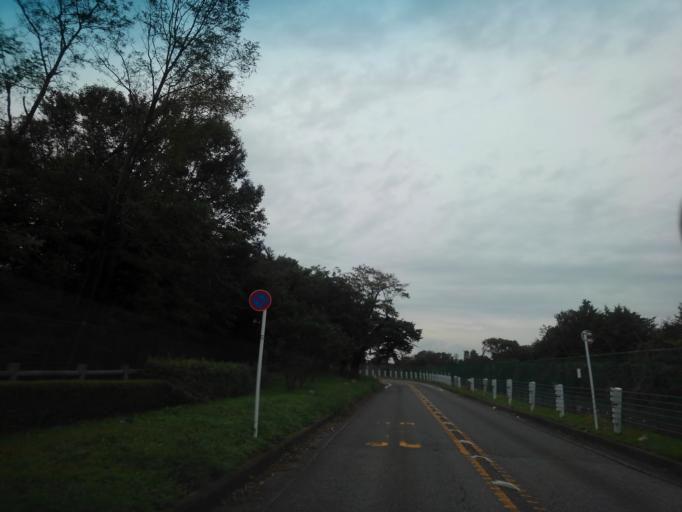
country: JP
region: Tokyo
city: Higashimurayama-shi
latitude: 35.7674
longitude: 139.4258
